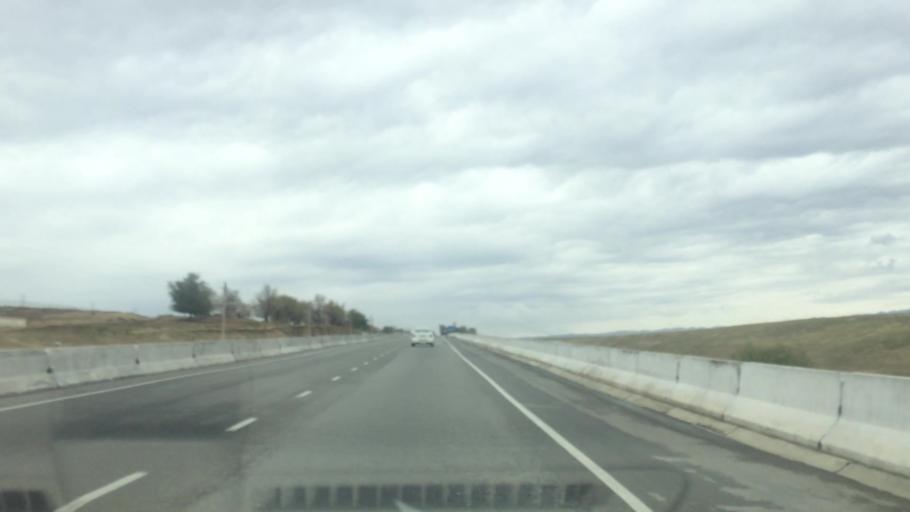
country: UZ
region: Samarqand
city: Bulung'ur
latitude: 39.9478
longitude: 67.5351
